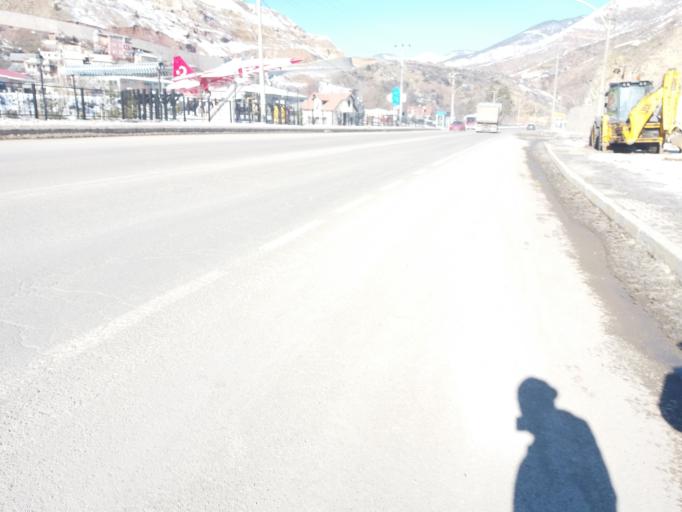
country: TR
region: Gumushane
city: Gumushkhane
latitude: 40.4392
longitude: 39.5042
